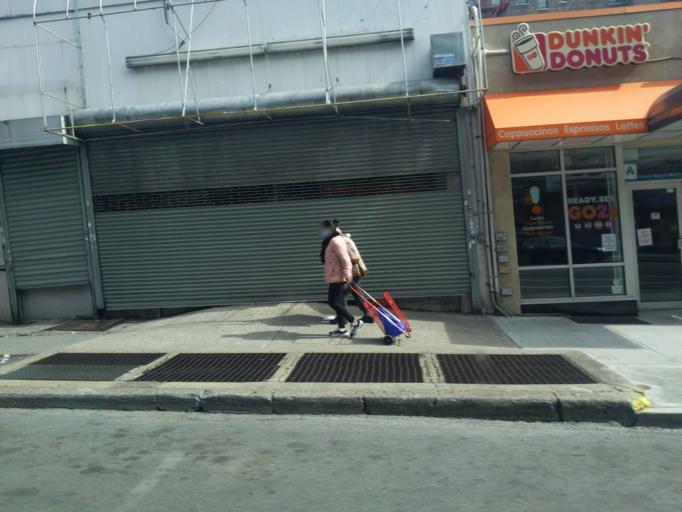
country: US
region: New York
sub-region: Queens County
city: Long Island City
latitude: 40.7433
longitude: -73.8835
